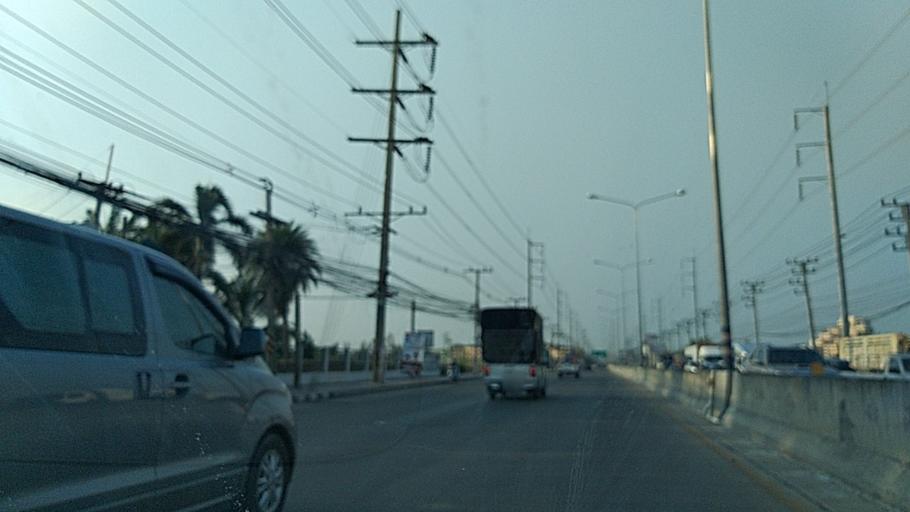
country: TH
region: Phra Nakhon Si Ayutthaya
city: Ban Bang Kadi Pathum Thani
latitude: 13.9768
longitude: 100.5506
